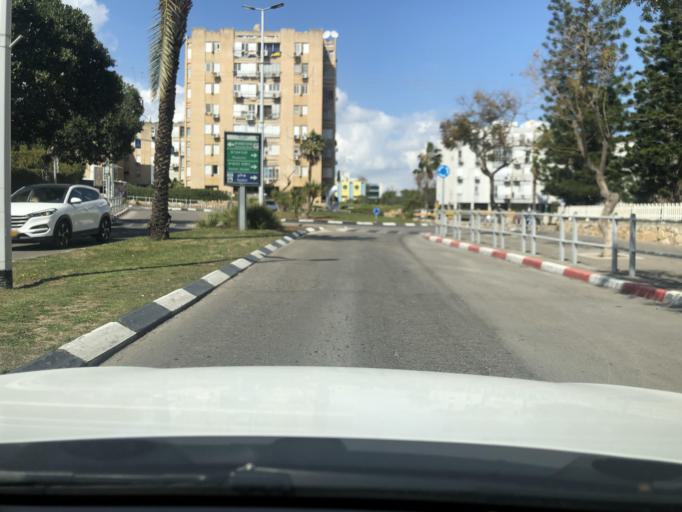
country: IL
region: Tel Aviv
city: Bat Yam
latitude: 32.0090
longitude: 34.7551
